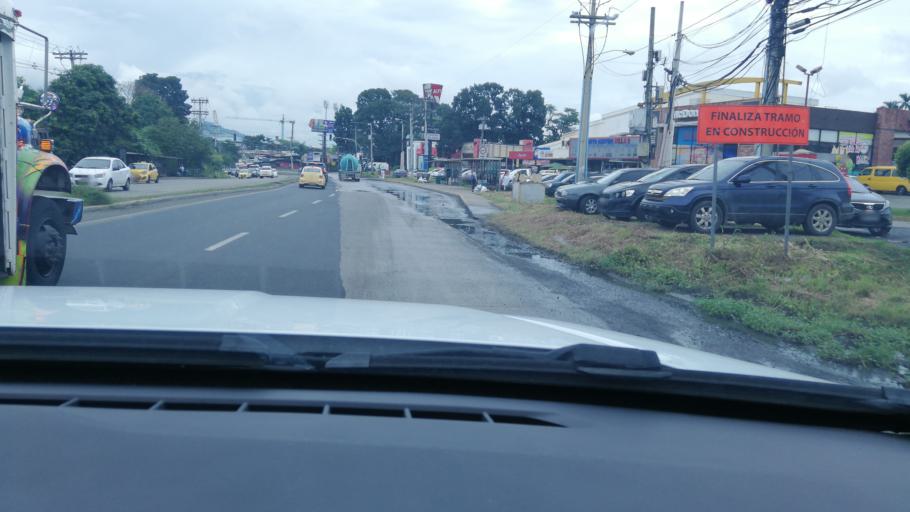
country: PA
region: Panama
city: Las Cumbres
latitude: 9.0682
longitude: -79.5183
